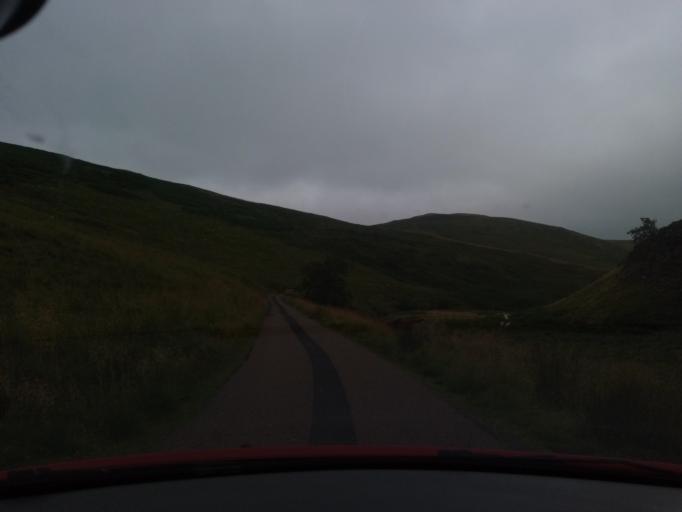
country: GB
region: England
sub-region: Northumberland
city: Rochester
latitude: 55.3945
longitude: -2.2298
